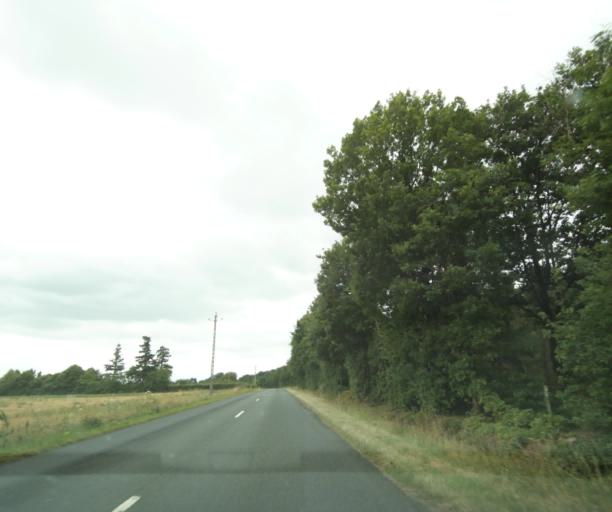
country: FR
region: Pays de la Loire
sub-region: Departement de la Sarthe
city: Precigne
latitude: 47.7946
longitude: -0.3209
